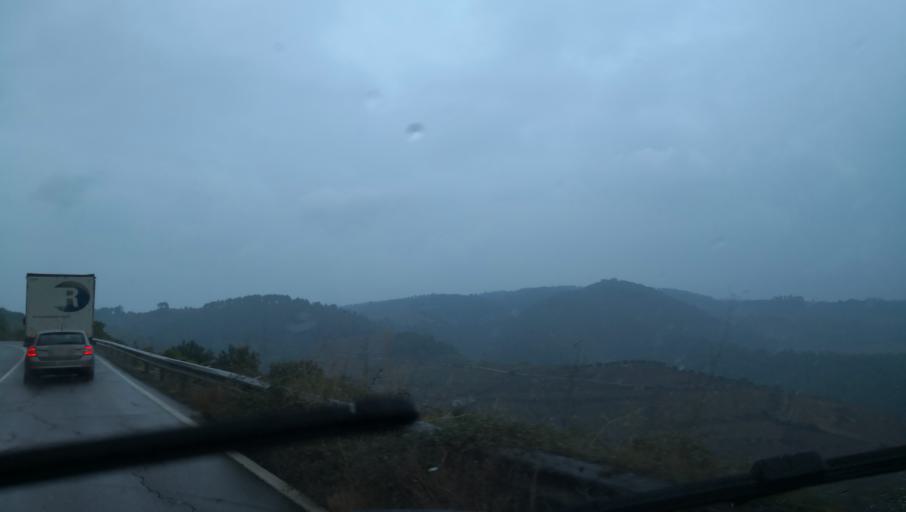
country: PT
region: Vila Real
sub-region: Vila Real
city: Vila Real
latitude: 41.2288
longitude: -7.7269
